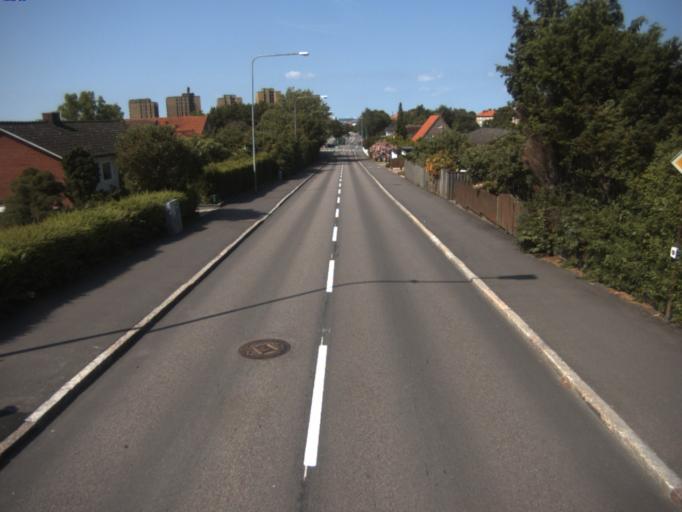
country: SE
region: Skane
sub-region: Helsingborg
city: Helsingborg
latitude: 56.0309
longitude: 12.7308
